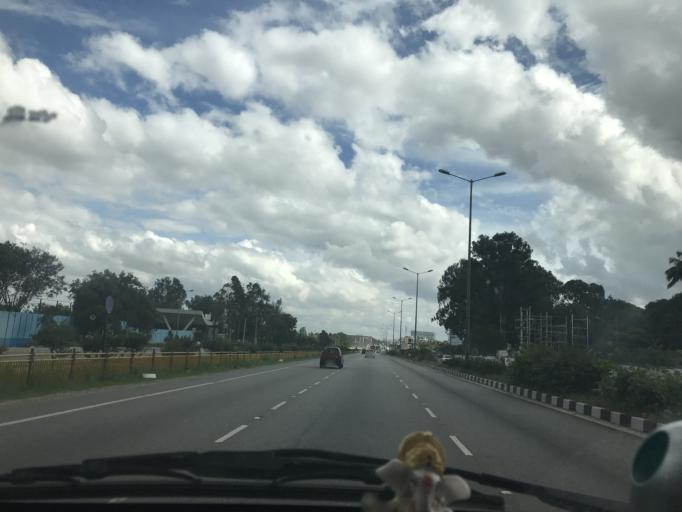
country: IN
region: Karnataka
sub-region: Bangalore Urban
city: Yelahanka
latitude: 13.1292
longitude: 77.6144
